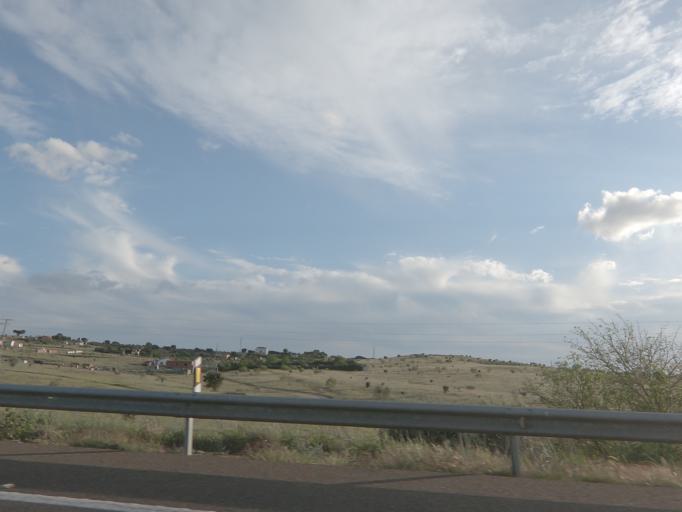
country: ES
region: Extremadura
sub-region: Provincia de Badajoz
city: Badajoz
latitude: 38.8792
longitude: -6.8856
